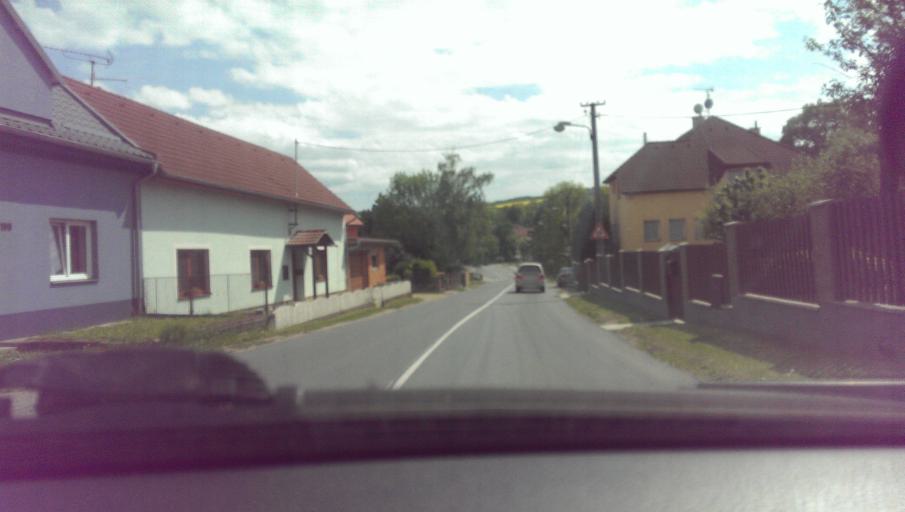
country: CZ
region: Zlin
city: Bilovice
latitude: 49.1010
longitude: 17.5474
